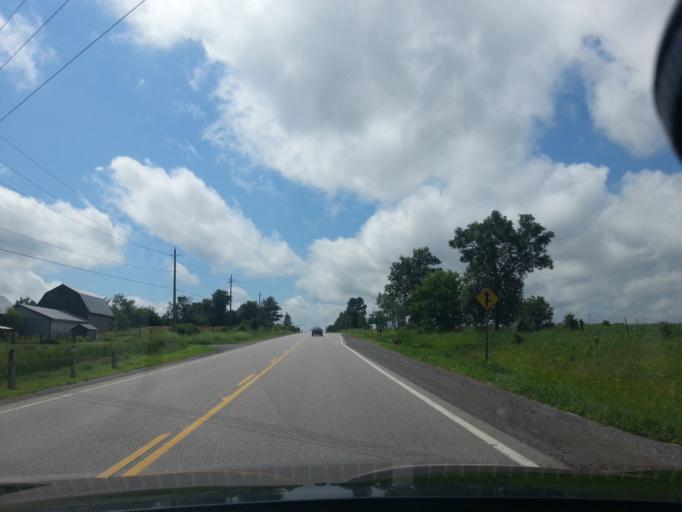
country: CA
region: Ontario
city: Renfrew
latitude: 45.5211
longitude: -76.8614
